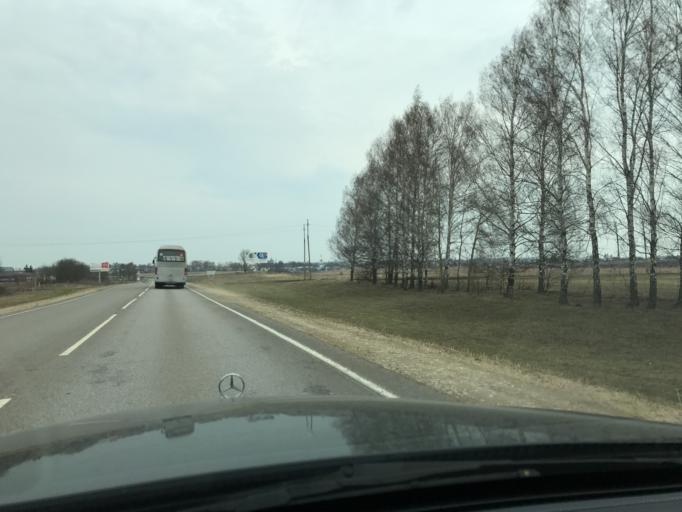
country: RU
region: Vladimir
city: Suzdal'
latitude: 56.3982
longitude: 40.4490
